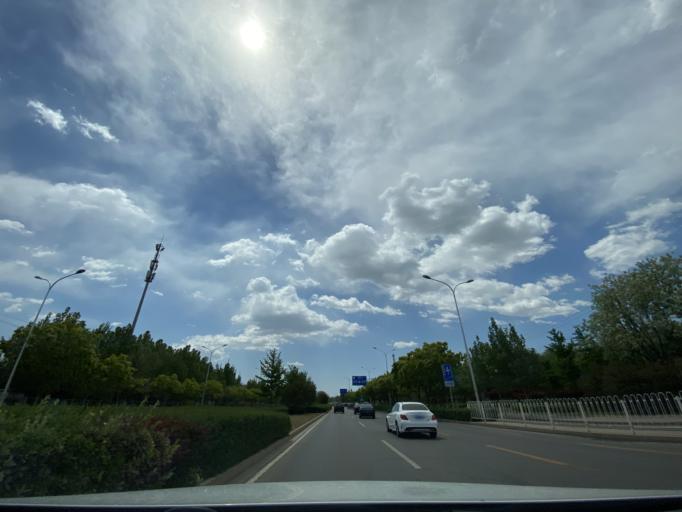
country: CN
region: Beijing
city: Sijiqing
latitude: 39.9415
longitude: 116.2404
